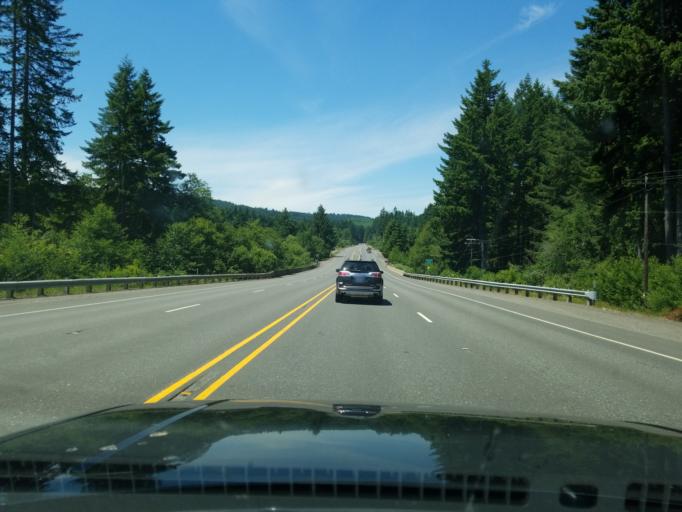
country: US
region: Oregon
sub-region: Columbia County
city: Vernonia
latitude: 45.7586
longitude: -123.2955
